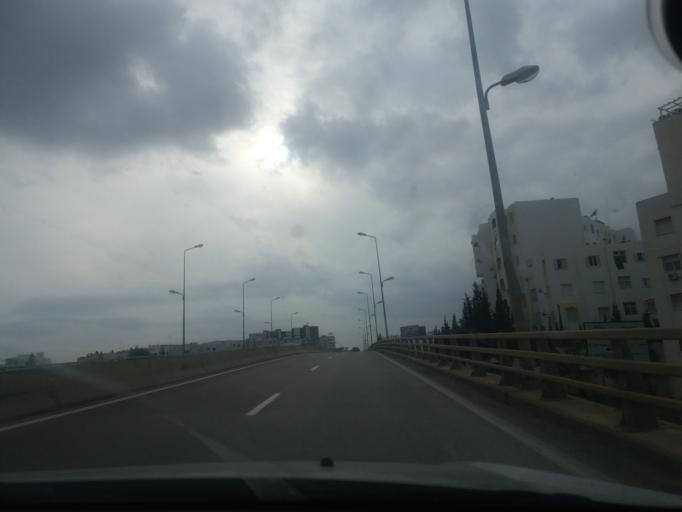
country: TN
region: Ariana
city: Ariana
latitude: 36.8584
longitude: 10.1681
